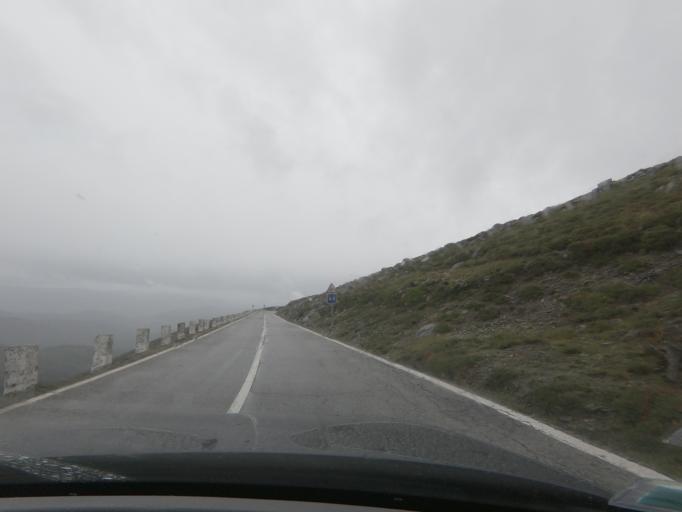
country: PT
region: Vila Real
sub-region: Mondim de Basto
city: Mondim de Basto
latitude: 41.3207
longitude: -7.8865
